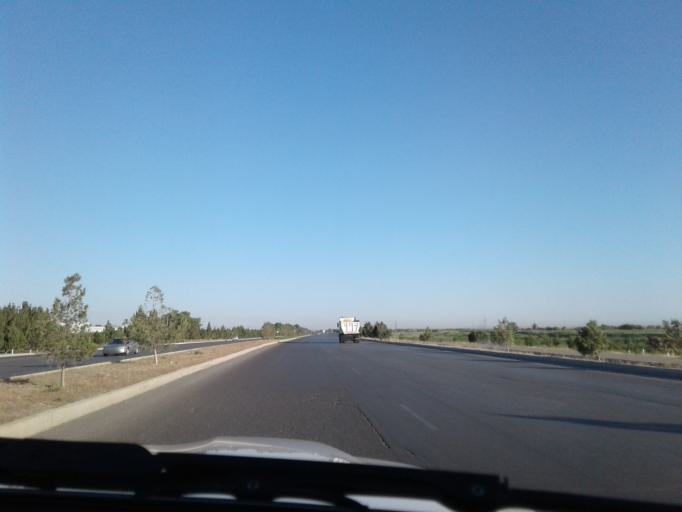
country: TM
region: Ahal
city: Abadan
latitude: 38.0643
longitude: 58.2572
